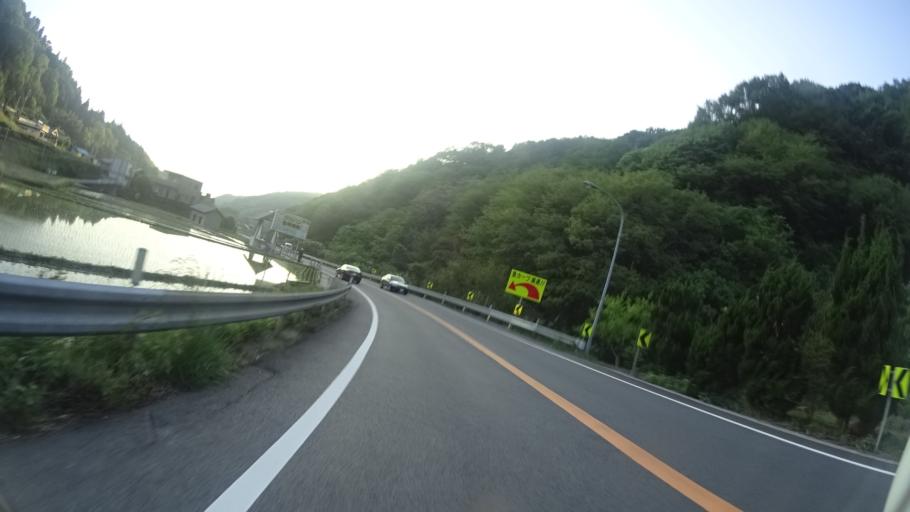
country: JP
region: Ehime
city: Kawanoecho
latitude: 33.9970
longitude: 133.6605
